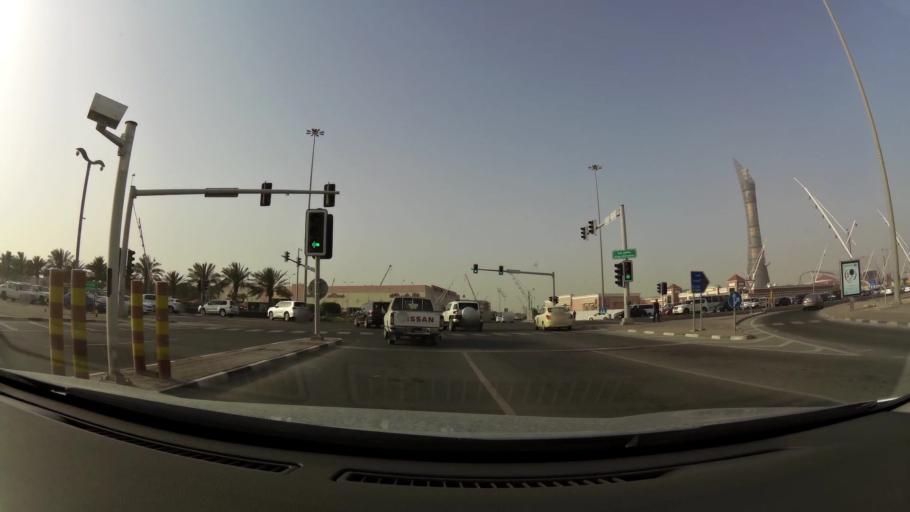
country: QA
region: Baladiyat ar Rayyan
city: Ar Rayyan
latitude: 25.2554
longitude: 51.4403
